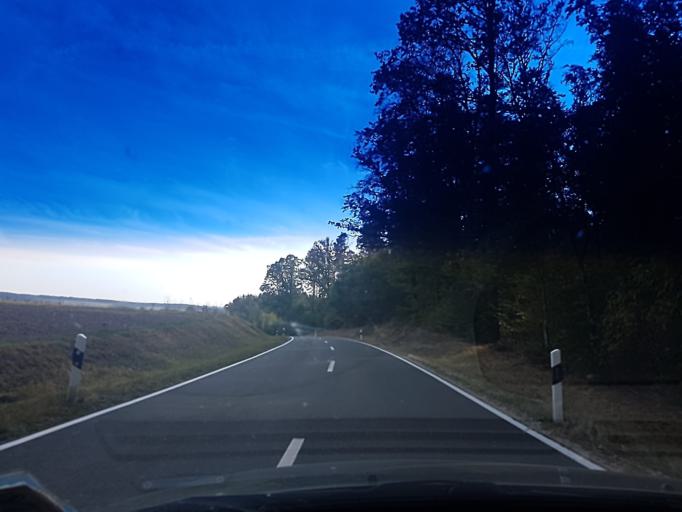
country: DE
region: Bavaria
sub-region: Upper Franconia
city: Burgwindheim
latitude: 49.7869
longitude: 10.5650
